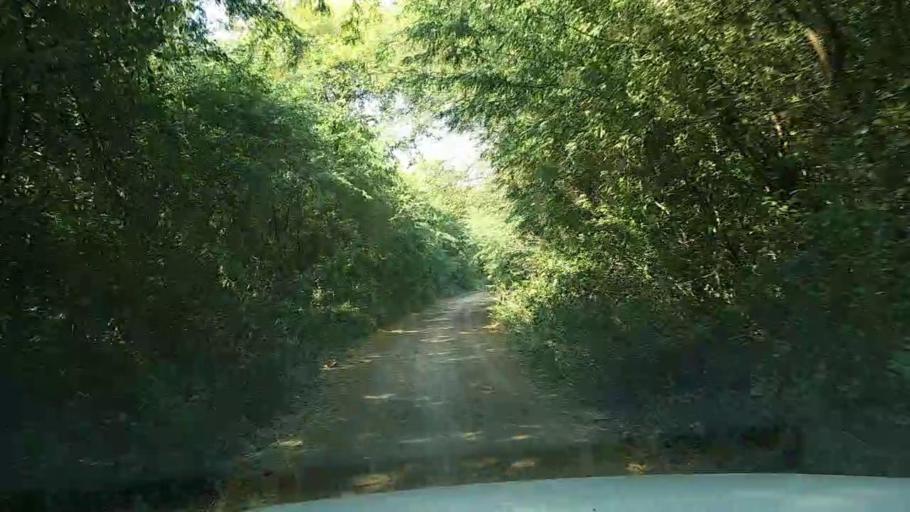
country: PK
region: Sindh
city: Daro Mehar
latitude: 24.6960
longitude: 68.1638
